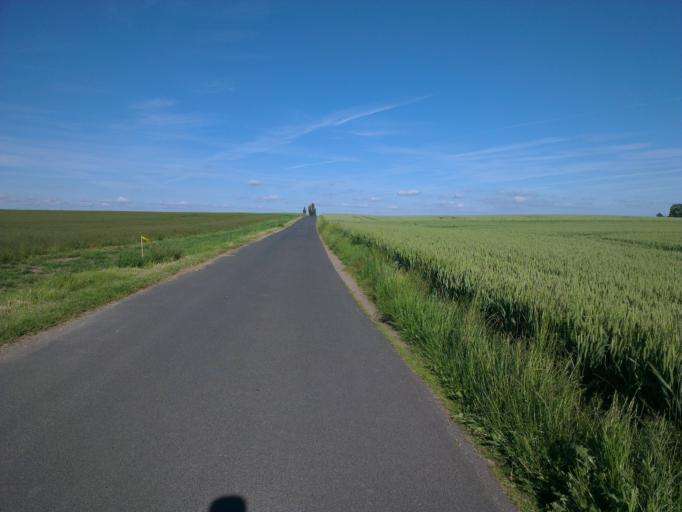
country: DK
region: Capital Region
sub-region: Frederikssund Kommune
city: Skibby
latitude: 55.7568
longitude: 11.9802
